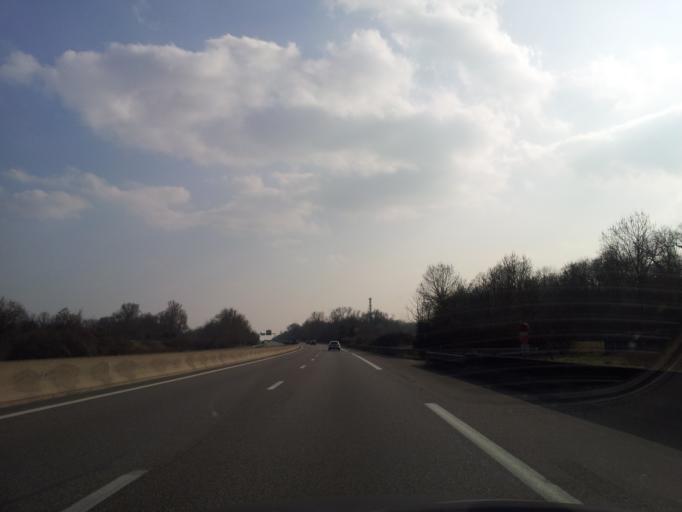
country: FR
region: Alsace
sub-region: Departement du Haut-Rhin
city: Colmar
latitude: 48.0457
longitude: 7.3704
